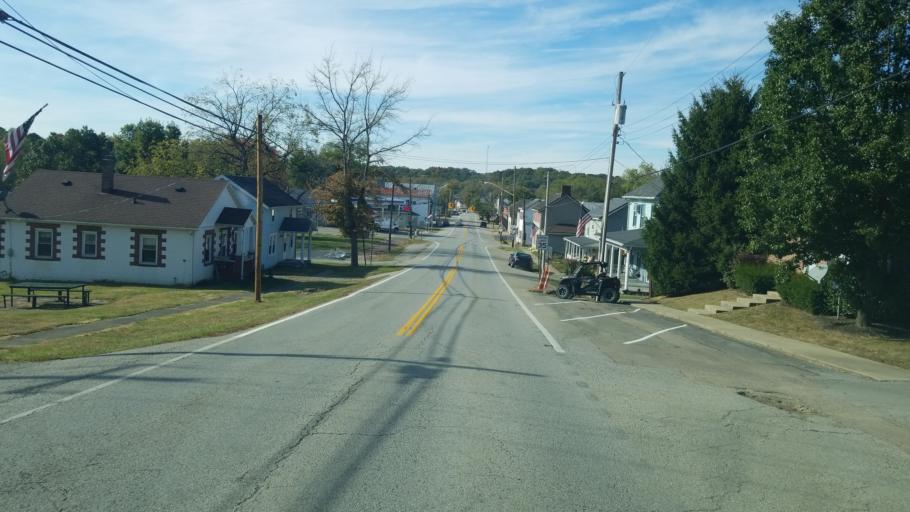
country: US
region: Ohio
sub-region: Clinton County
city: Blanchester
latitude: 39.4002
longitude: -83.9792
